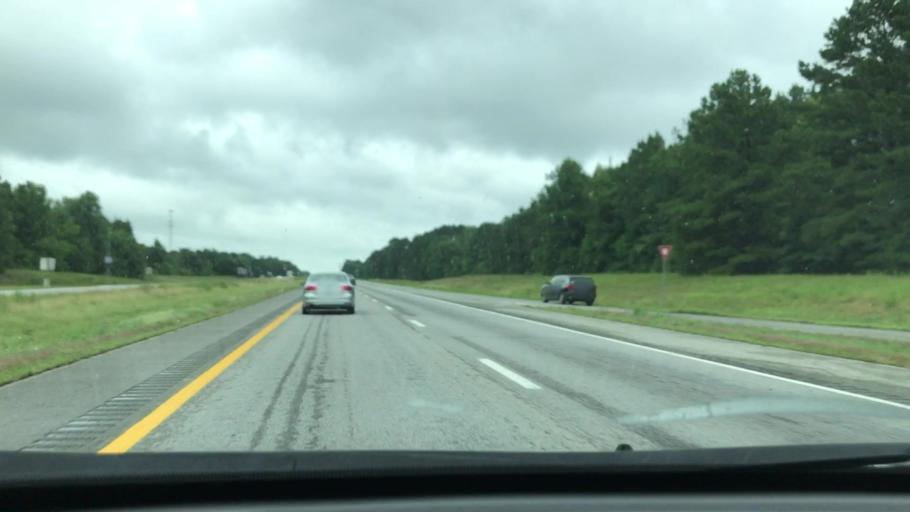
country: US
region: Virginia
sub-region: City of Emporia
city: Emporia
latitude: 36.8072
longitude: -77.4583
